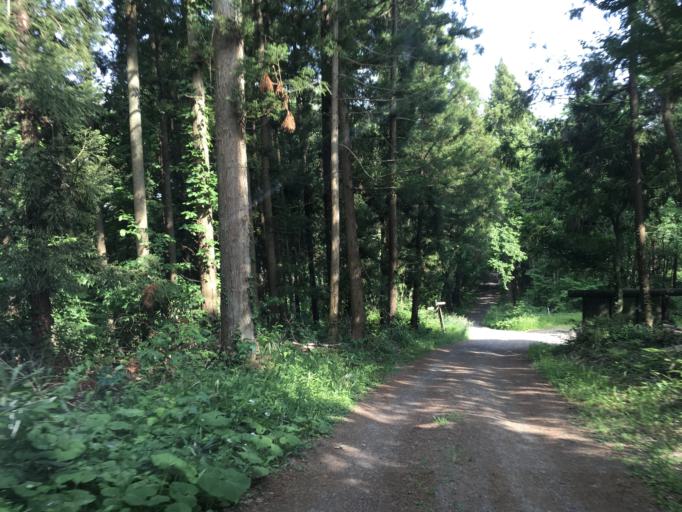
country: JP
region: Iwate
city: Hanamaki
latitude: 39.4013
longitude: 141.1616
